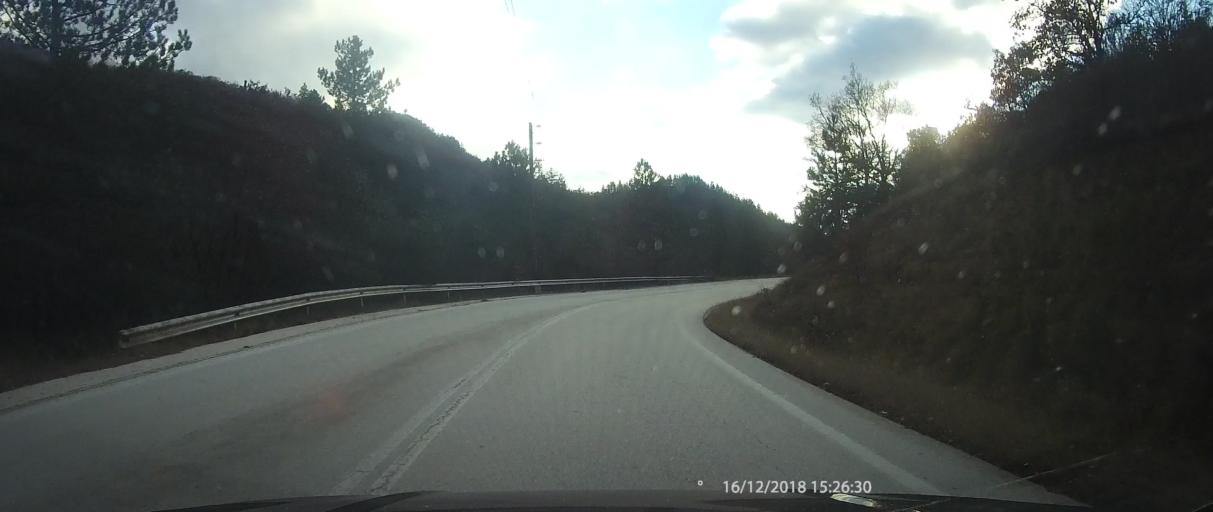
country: GR
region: Epirus
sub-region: Nomos Ioanninon
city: Konitsa
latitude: 40.1166
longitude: 20.7795
